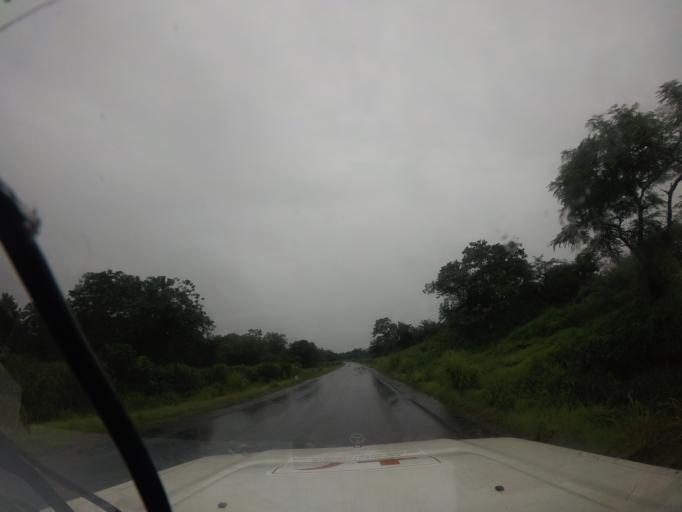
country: SL
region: Northern Province
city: Binkolo
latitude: 9.0737
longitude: -11.9500
